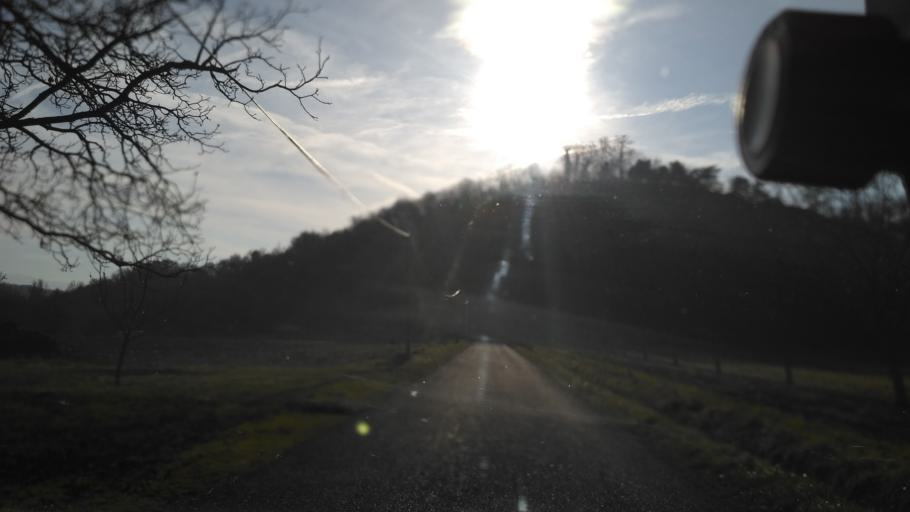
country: FR
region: Rhone-Alpes
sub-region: Departement de la Drome
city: Saint-Paul-les-Romans
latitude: 45.1215
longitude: 5.1476
